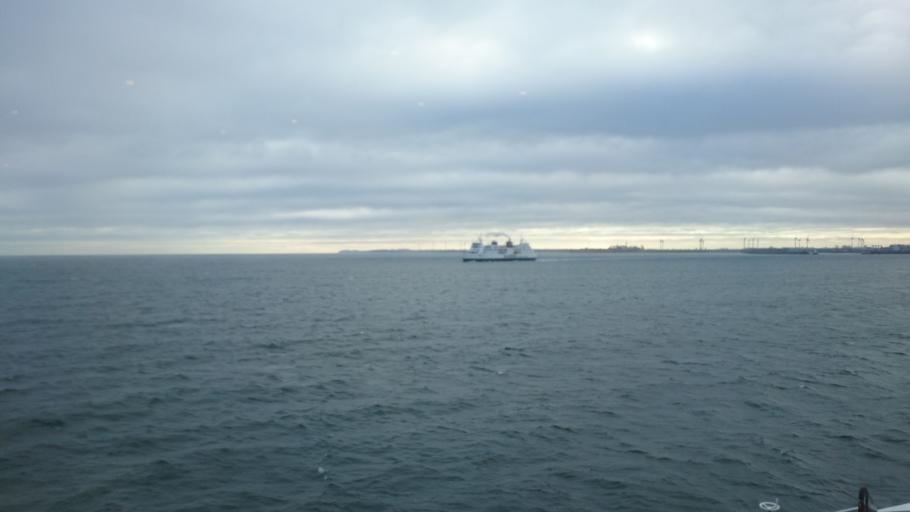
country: DE
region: Schleswig-Holstein
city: Fehmarn
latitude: 54.5215
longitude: 11.2404
